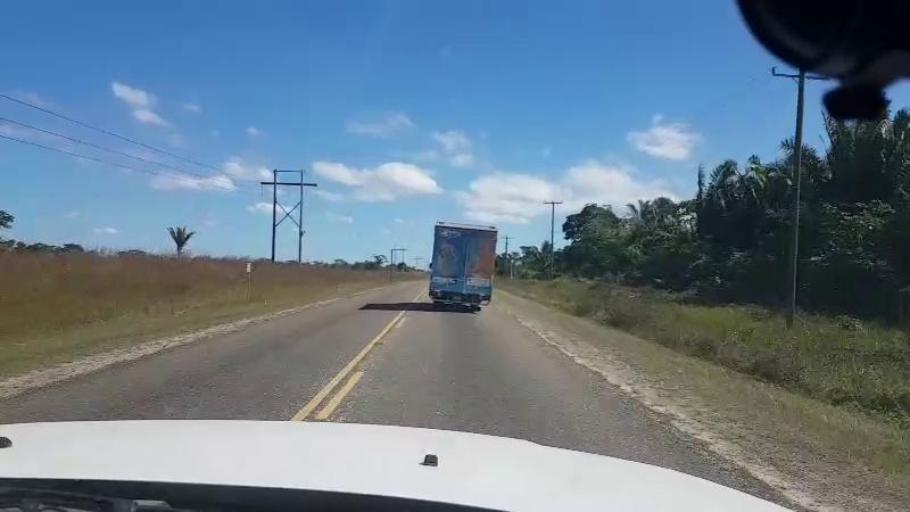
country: BZ
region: Cayo
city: Belmopan
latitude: 17.2767
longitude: -88.7378
